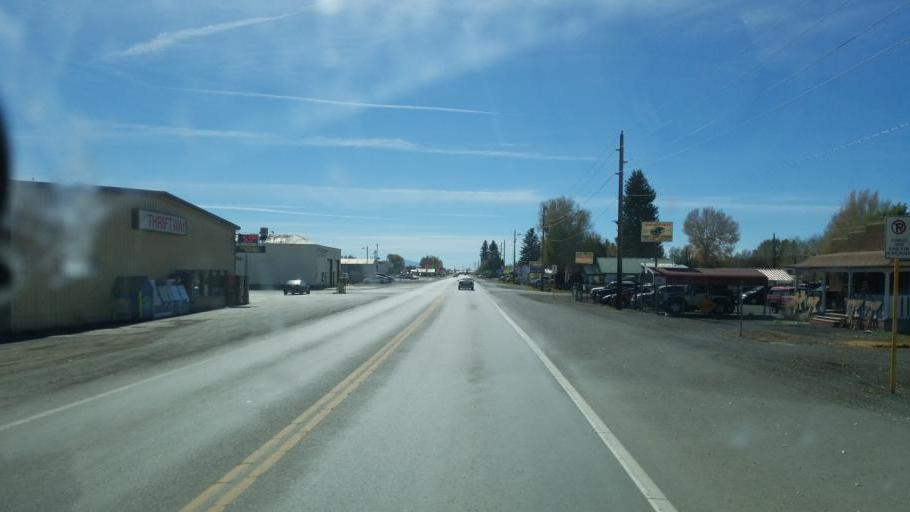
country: US
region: Colorado
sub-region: Conejos County
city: Conejos
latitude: 37.2780
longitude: -105.9611
